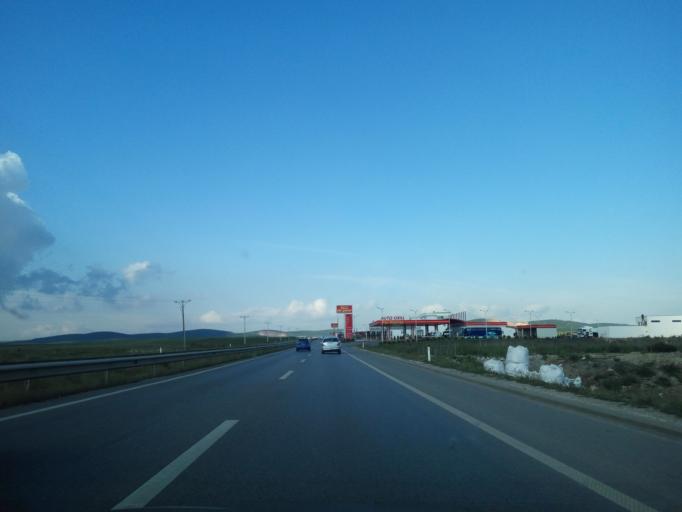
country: XK
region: Pristina
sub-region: Komuna e Drenasit
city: Glogovac
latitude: 42.5865
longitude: 20.9114
